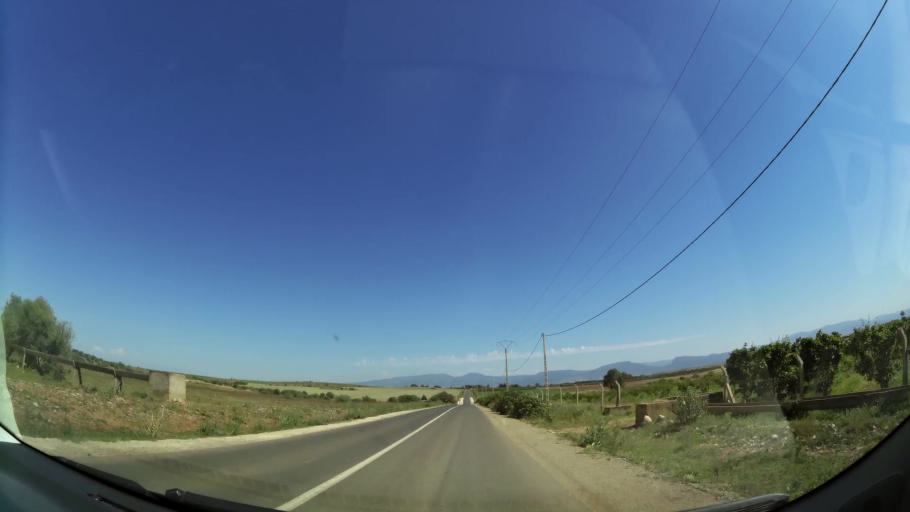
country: MA
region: Oriental
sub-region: Berkane-Taourirt
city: Madagh
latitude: 35.0354
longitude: -2.4188
